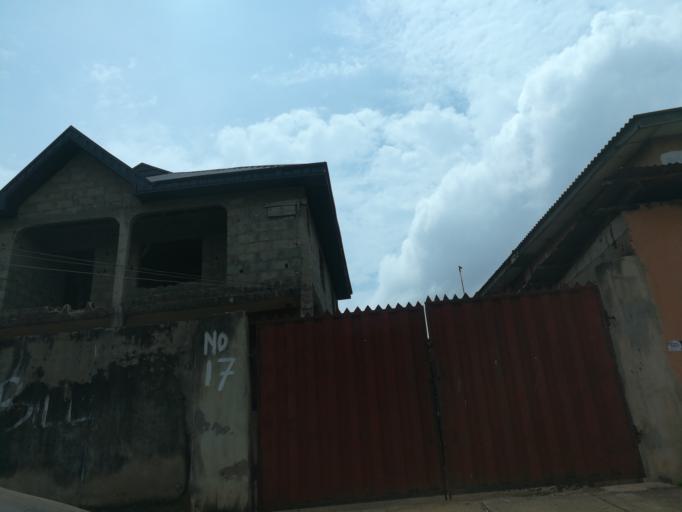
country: NG
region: Lagos
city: Oshodi
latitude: 6.5527
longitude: 3.3236
